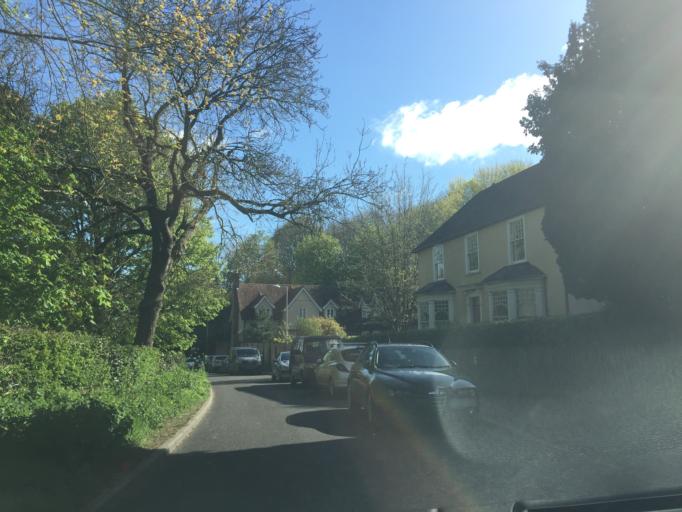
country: GB
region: England
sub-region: Essex
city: Harlow
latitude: 51.7754
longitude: 0.0981
